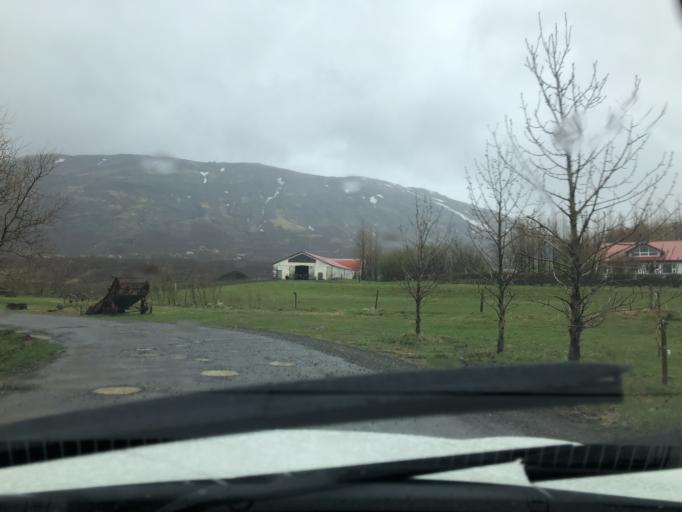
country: IS
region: South
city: Selfoss
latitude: 64.2425
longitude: -20.5489
